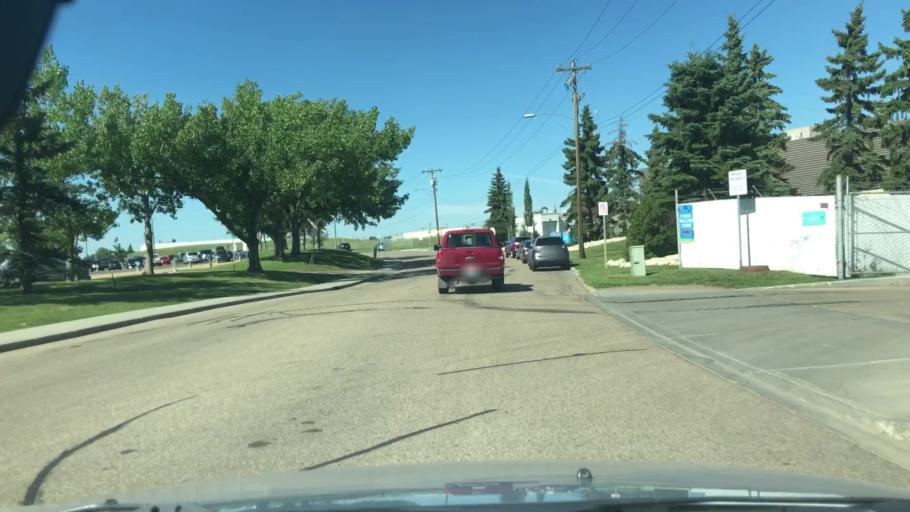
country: CA
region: Alberta
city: Edmonton
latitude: 53.5353
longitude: -113.4147
